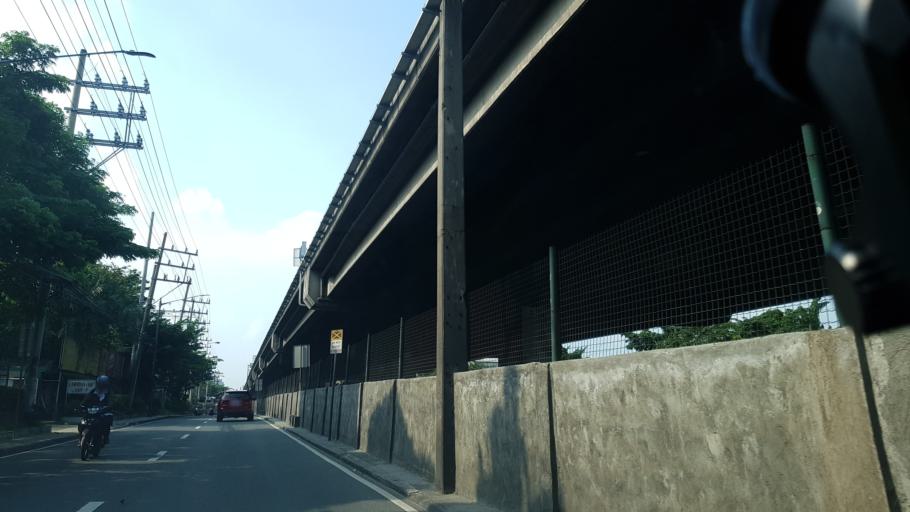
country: PH
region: Calabarzon
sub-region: Province of Rizal
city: Taguig
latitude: 14.4972
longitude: 121.0399
